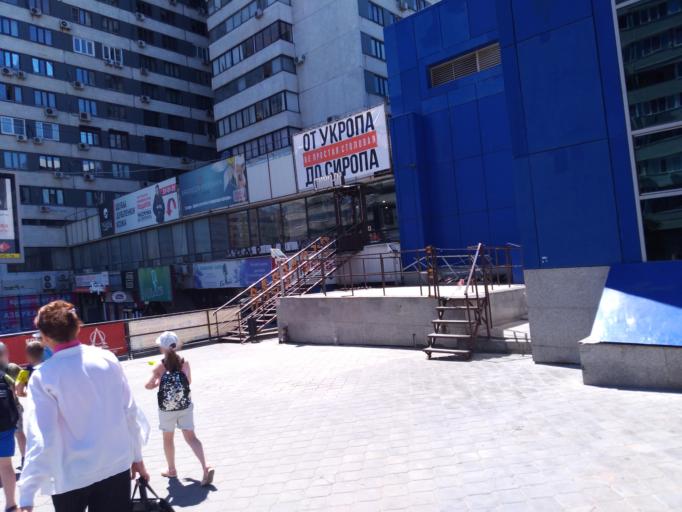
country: RU
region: Volgograd
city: Volgograd
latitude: 48.7043
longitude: 44.5101
